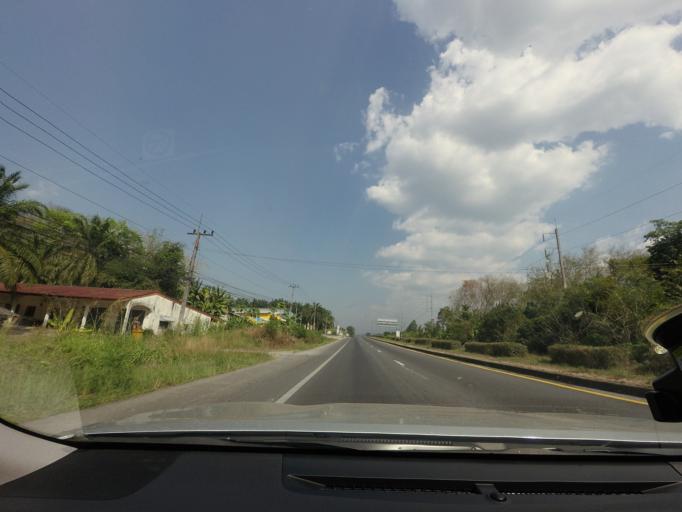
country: TH
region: Phangnga
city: Thap Put
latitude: 8.5081
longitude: 98.6664
